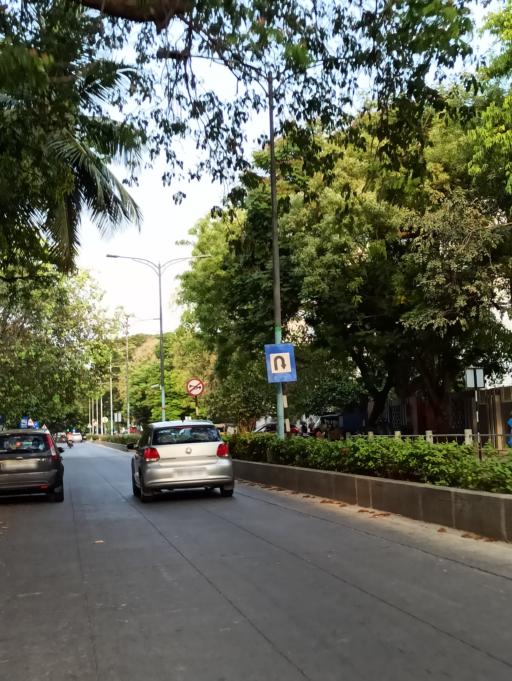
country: IN
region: Tamil Nadu
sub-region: Chennai
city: Chetput
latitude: 13.0693
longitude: 80.2357
